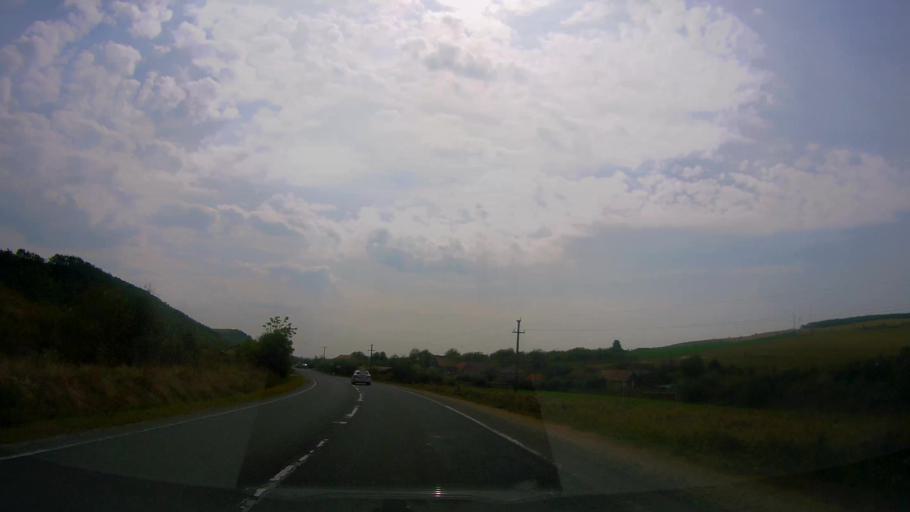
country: RO
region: Cluj
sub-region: Comuna Sanpaul
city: Sanpaul
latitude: 46.8353
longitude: 23.4077
